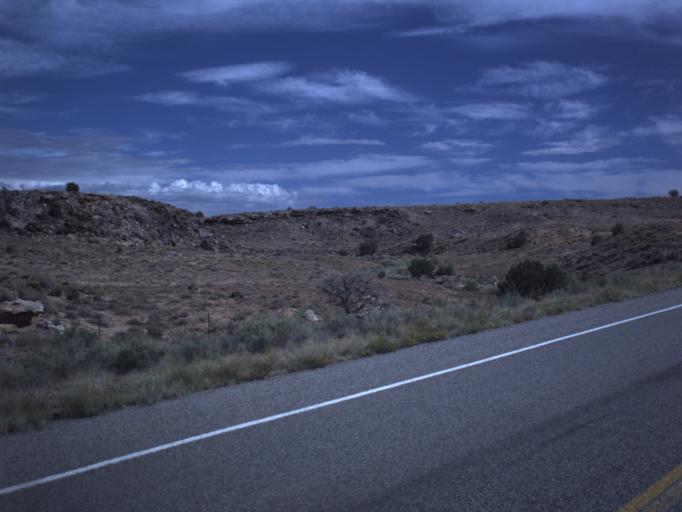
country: US
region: Colorado
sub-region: Montezuma County
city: Towaoc
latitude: 37.1822
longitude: -109.1256
